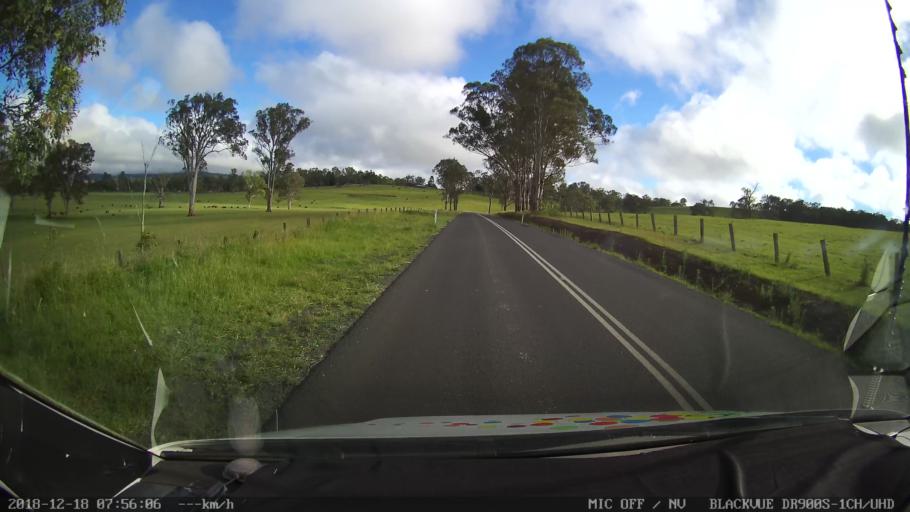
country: AU
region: New South Wales
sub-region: Kyogle
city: Kyogle
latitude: -28.4019
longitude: 152.6041
